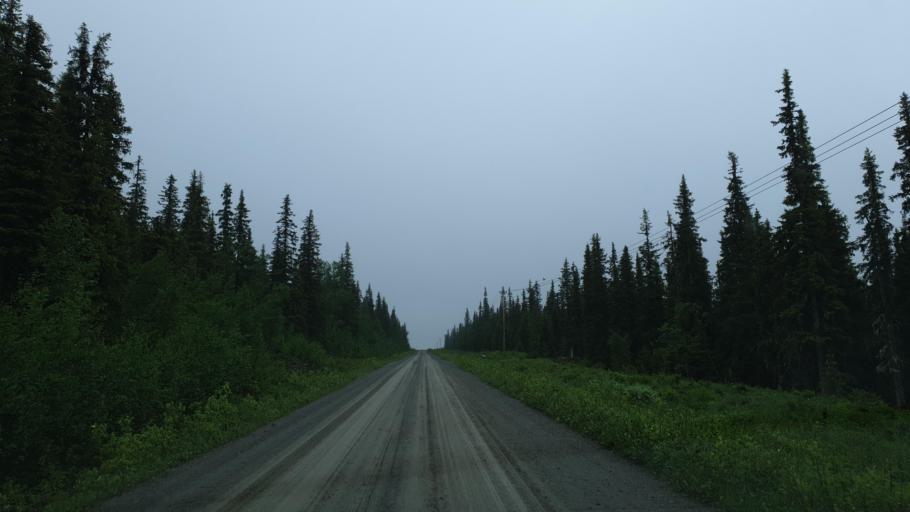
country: SE
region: Vaesterbotten
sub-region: Vilhelmina Kommun
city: Sjoberg
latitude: 65.3191
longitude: 15.9447
